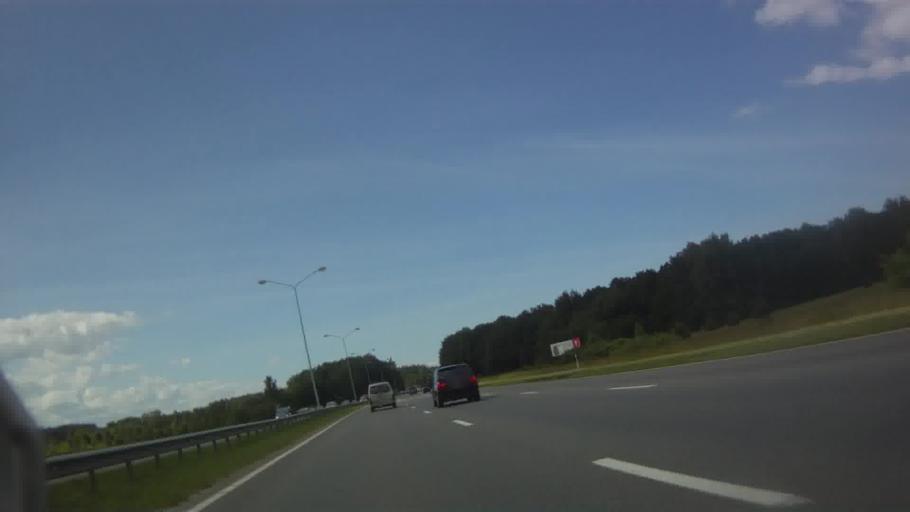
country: LV
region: Babite
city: Pinki
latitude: 56.9624
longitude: 23.8821
